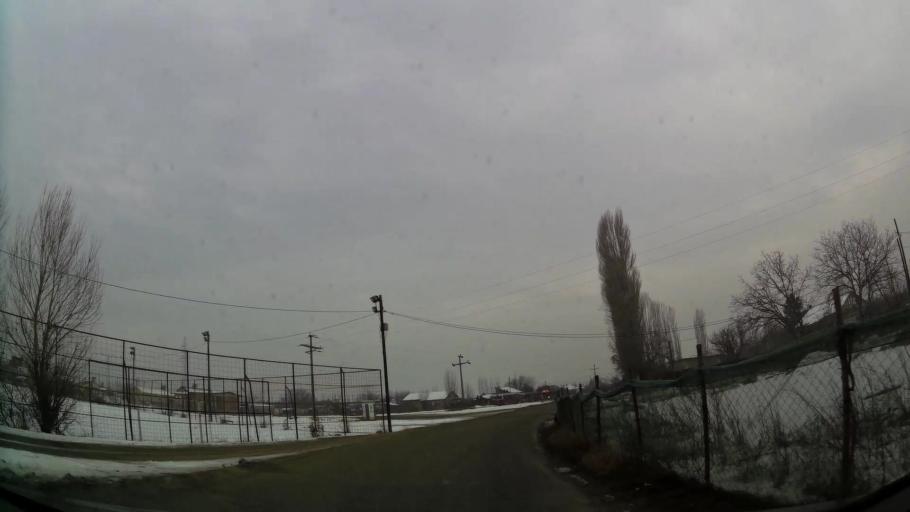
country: MK
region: Suto Orizari
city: Suto Orizare
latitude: 42.0463
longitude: 21.3659
